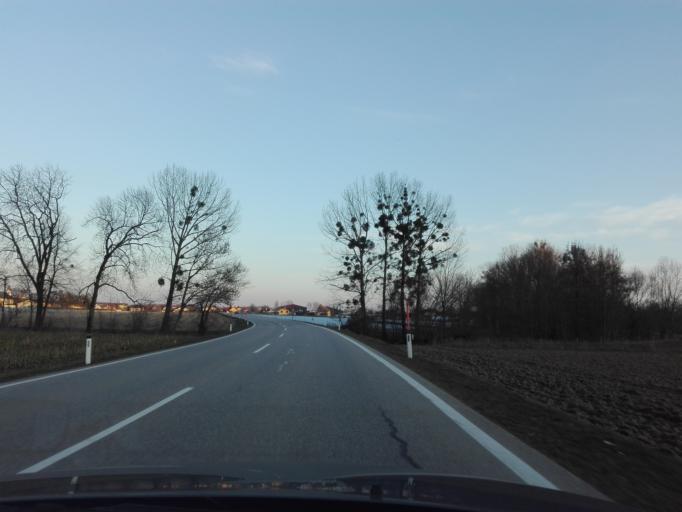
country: AT
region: Upper Austria
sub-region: Politischer Bezirk Urfahr-Umgebung
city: Feldkirchen an der Donau
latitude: 48.3638
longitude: 13.9862
